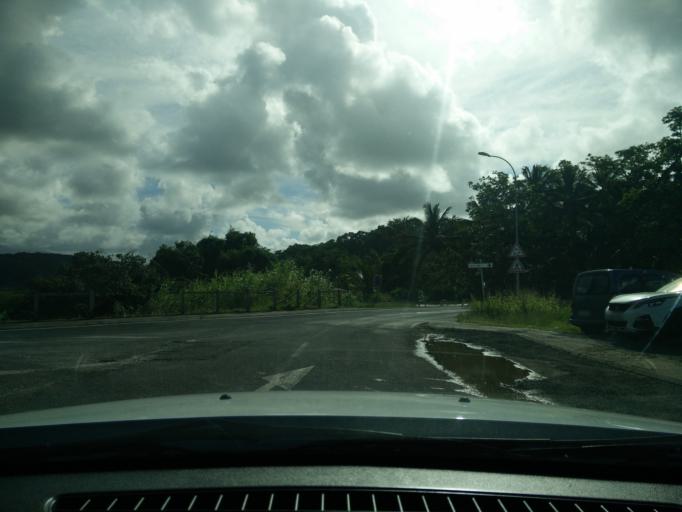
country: GP
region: Guadeloupe
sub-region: Guadeloupe
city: Petit-Bourg
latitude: 16.2026
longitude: -61.6088
